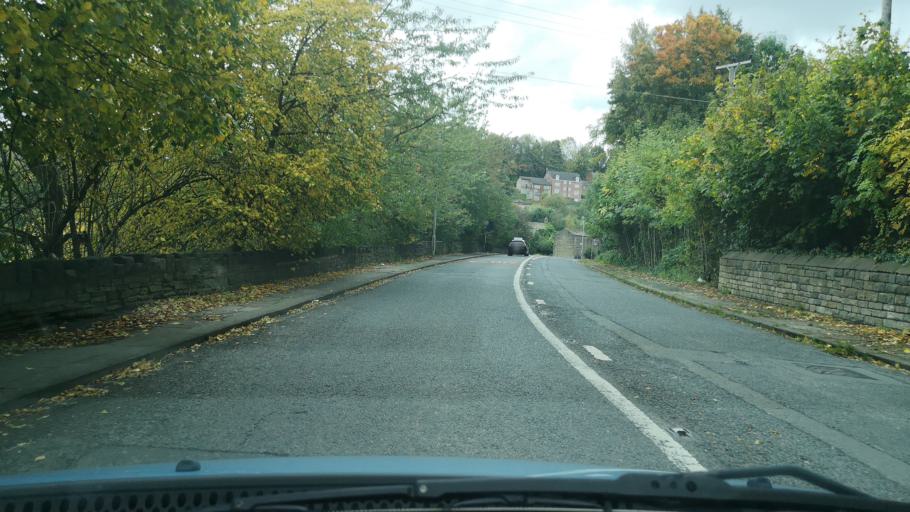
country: GB
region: England
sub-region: Kirklees
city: Dewsbury
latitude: 53.6691
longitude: -1.6201
